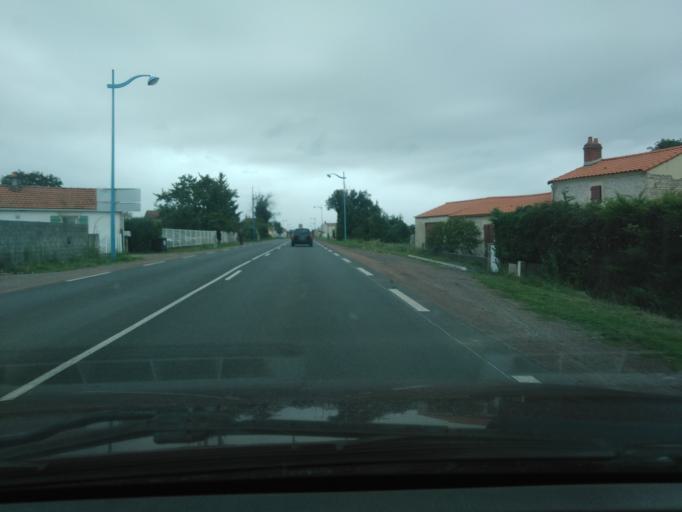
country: FR
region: Pays de la Loire
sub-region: Departement de la Vendee
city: Sainte-Gemme-la-Plaine
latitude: 46.4713
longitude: -1.1099
